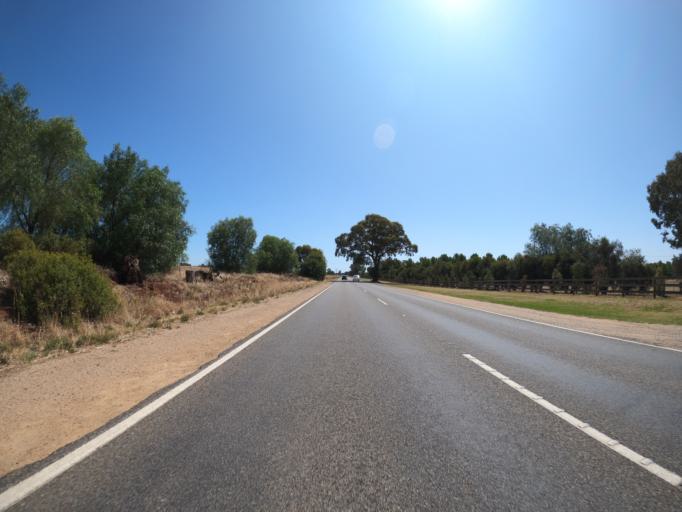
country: AU
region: Victoria
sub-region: Moira
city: Yarrawonga
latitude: -36.0259
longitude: 146.0935
